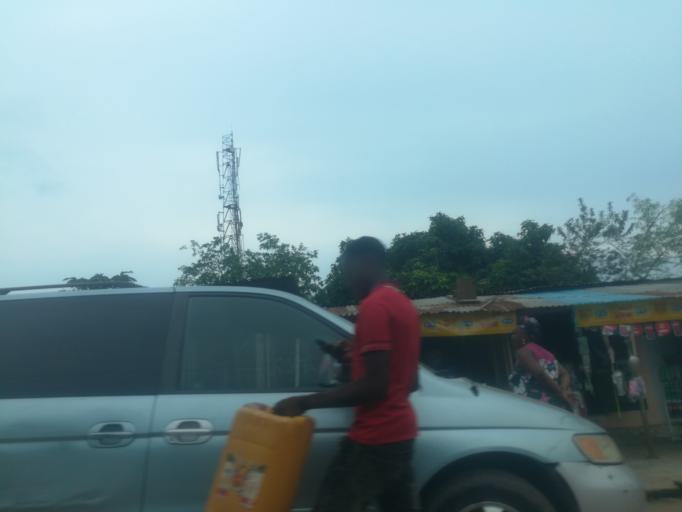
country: NG
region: Oyo
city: Ibadan
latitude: 7.3667
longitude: 3.8273
